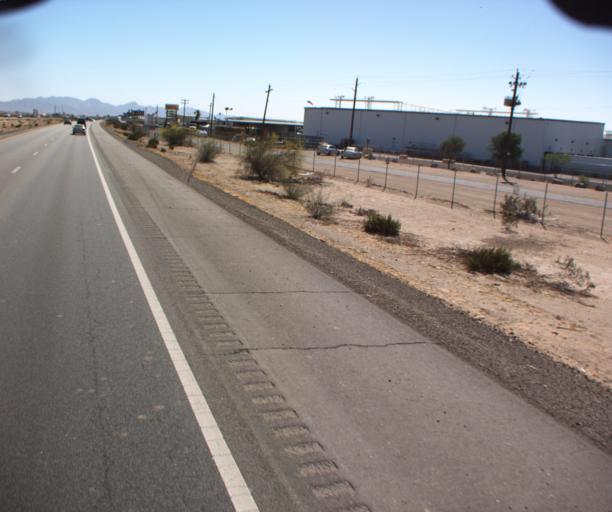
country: US
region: Arizona
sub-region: Yuma County
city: Yuma
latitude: 32.6847
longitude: -114.5640
